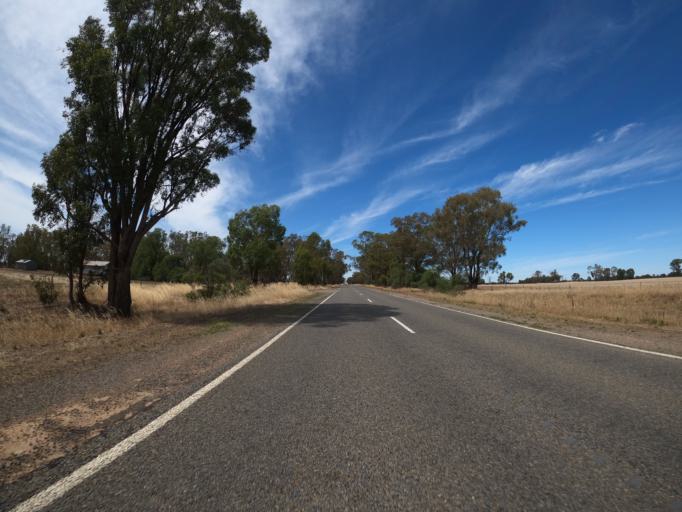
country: AU
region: Victoria
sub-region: Benalla
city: Benalla
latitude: -36.2921
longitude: 145.9523
